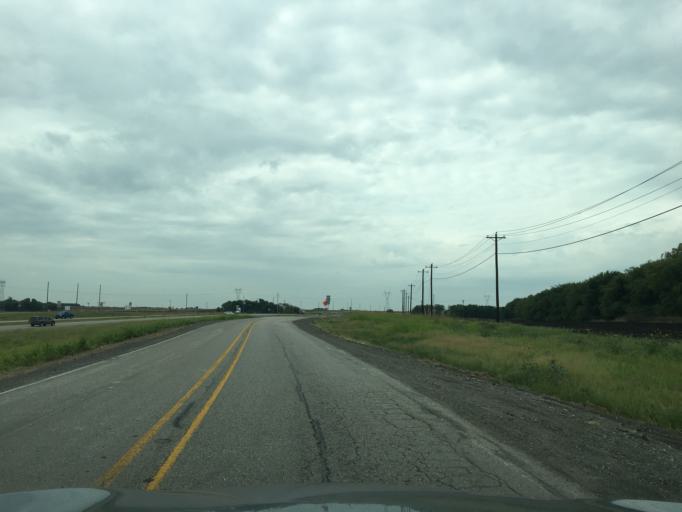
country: US
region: Texas
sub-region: Grayson County
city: Van Alstyne
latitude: 33.3815
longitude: -96.5820
